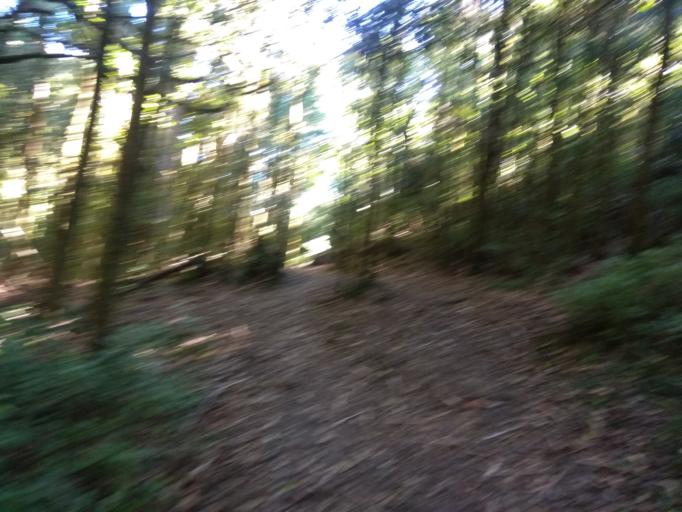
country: CR
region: Heredia
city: Santo Domingo
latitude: 10.1315
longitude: -84.1208
